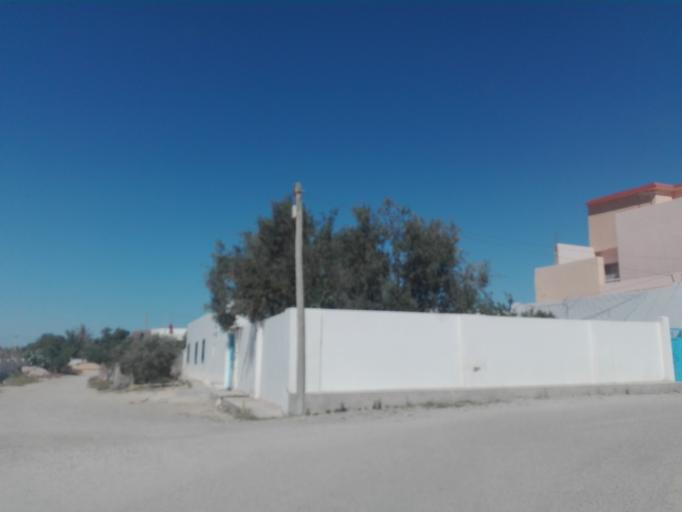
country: TN
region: Safaqis
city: Al Qarmadah
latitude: 34.7128
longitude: 11.1962
